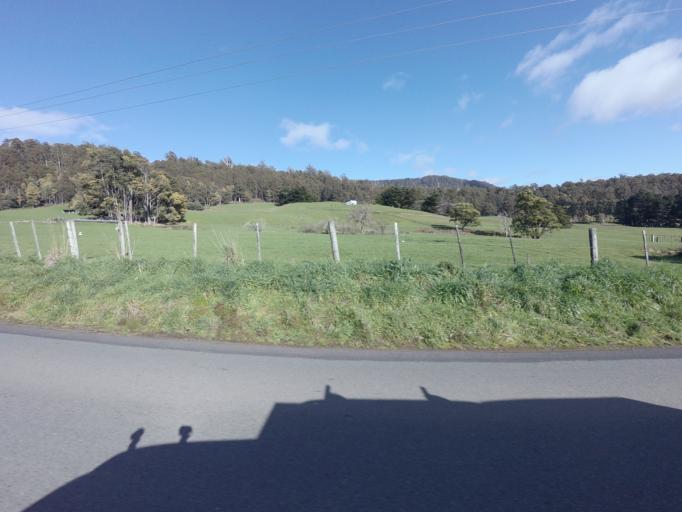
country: AU
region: Tasmania
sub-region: Huon Valley
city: Geeveston
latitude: -43.2423
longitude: 146.9921
